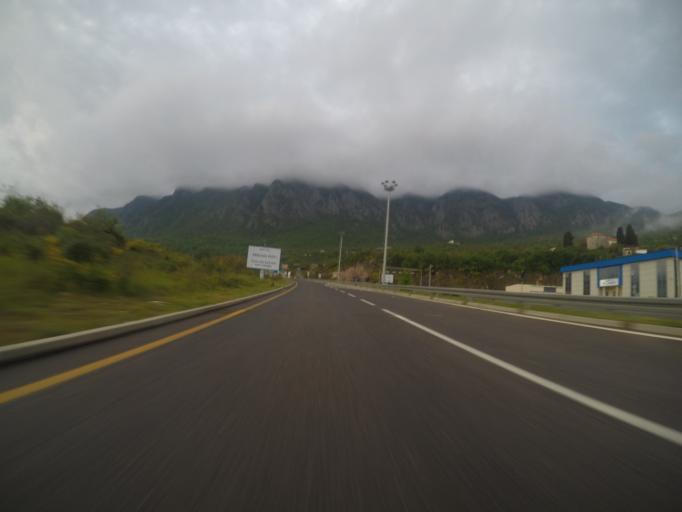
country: ME
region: Bar
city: Sutomore
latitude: 42.2033
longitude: 19.0507
